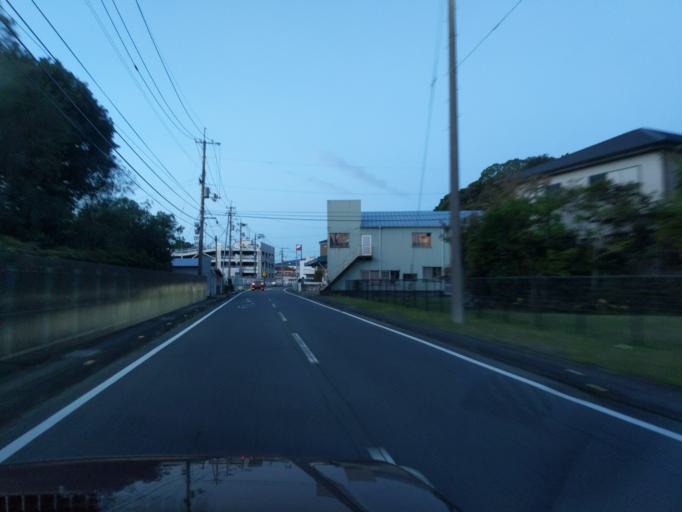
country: JP
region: Tokushima
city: Anan
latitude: 33.8794
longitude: 134.6511
